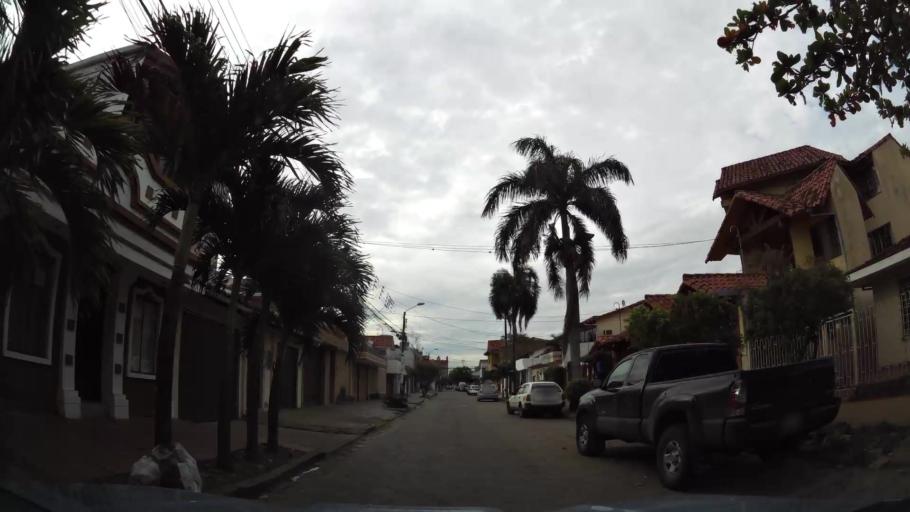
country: BO
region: Santa Cruz
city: Santa Cruz de la Sierra
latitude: -17.7891
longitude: -63.1741
